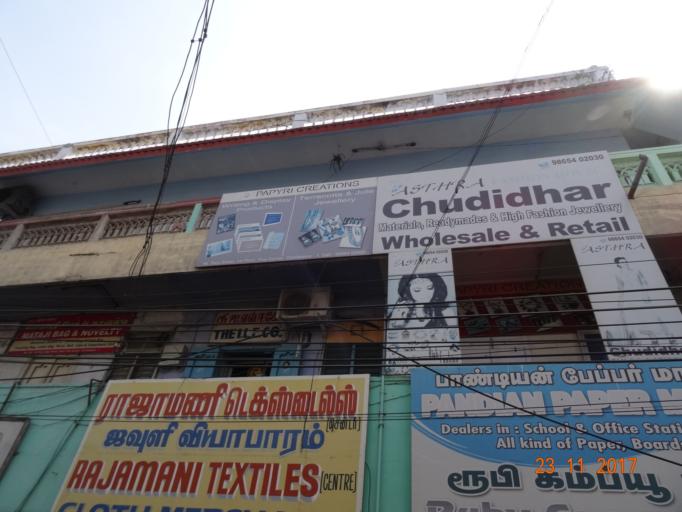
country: IN
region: Tamil Nadu
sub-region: Coimbatore
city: Coimbatore
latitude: 10.9953
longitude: 76.9605
